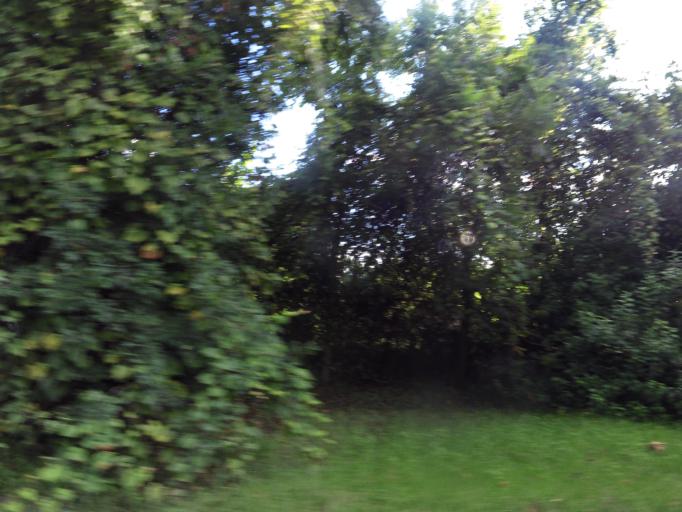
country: US
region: Florida
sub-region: Duval County
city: Jacksonville
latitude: 30.3262
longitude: -81.6820
